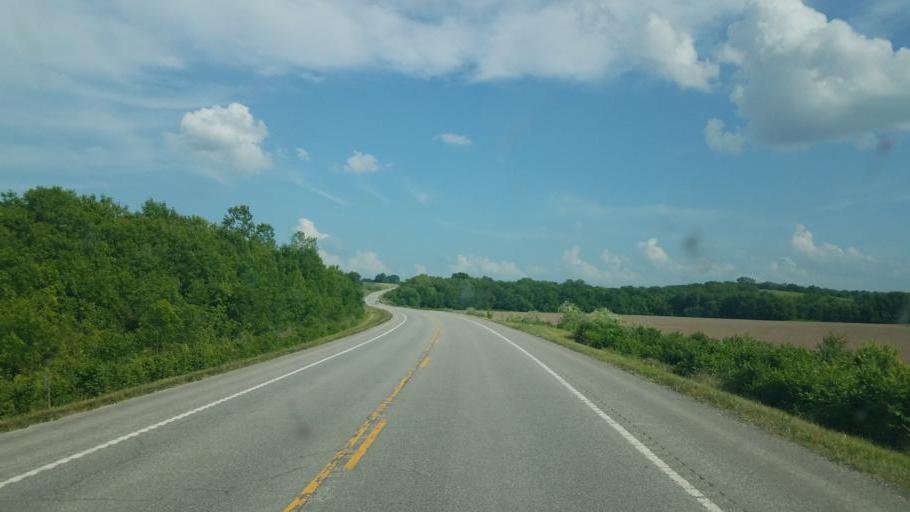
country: US
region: Missouri
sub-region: Cooper County
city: Boonville
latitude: 38.9025
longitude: -92.6727
